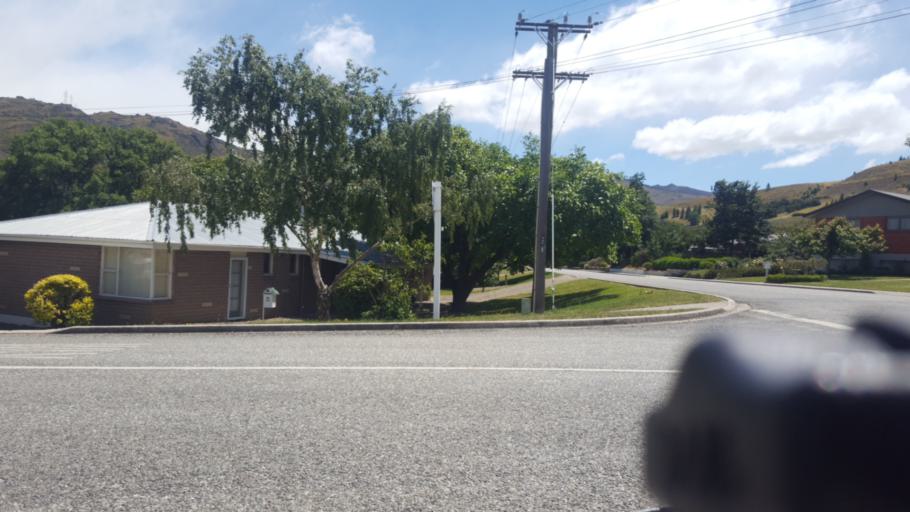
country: NZ
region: Otago
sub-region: Queenstown-Lakes District
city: Wanaka
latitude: -45.1900
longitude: 169.3225
